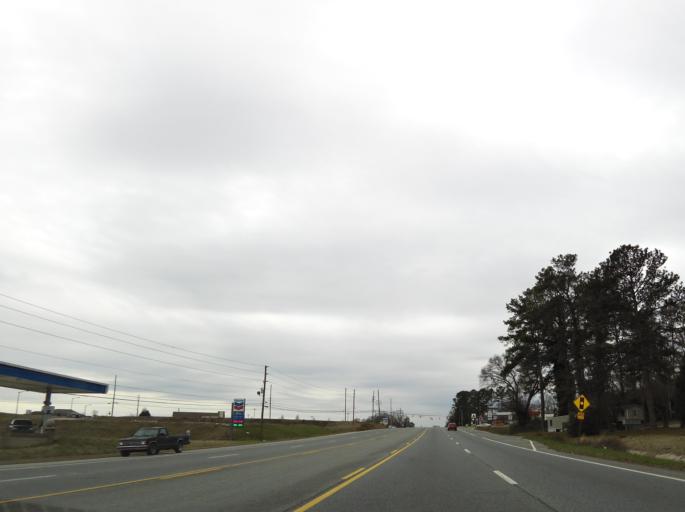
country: US
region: Georgia
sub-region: Houston County
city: Robins Air Force Base
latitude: 32.5705
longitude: -83.5932
